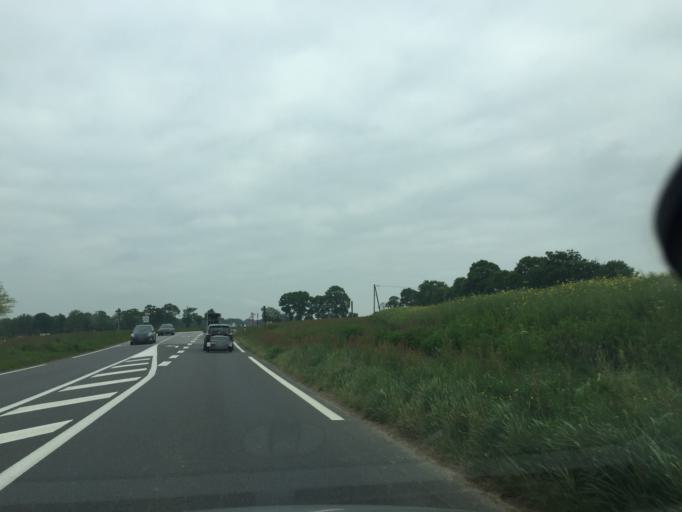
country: FR
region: Brittany
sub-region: Departement des Cotes-d'Armor
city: Henanbihen
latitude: 48.5293
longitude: -2.4215
